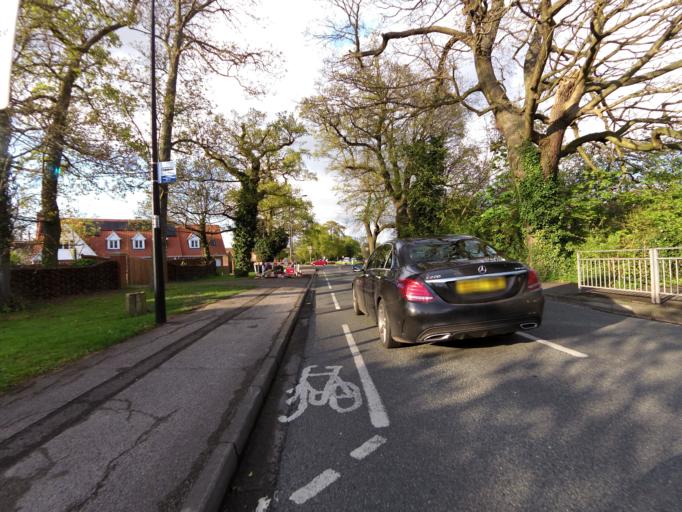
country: GB
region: England
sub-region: Suffolk
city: Ipswich
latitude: 52.0703
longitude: 1.1699
